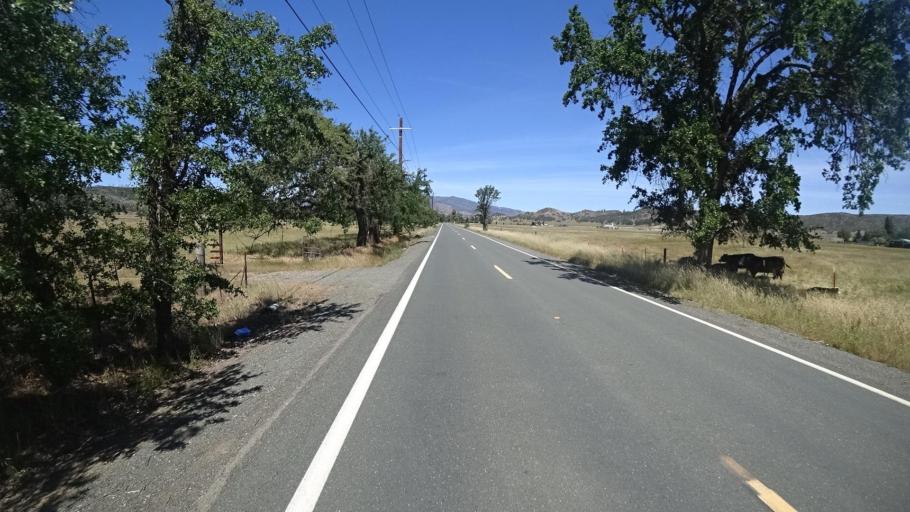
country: US
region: California
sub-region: Lake County
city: Middletown
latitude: 38.7433
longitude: -122.5741
